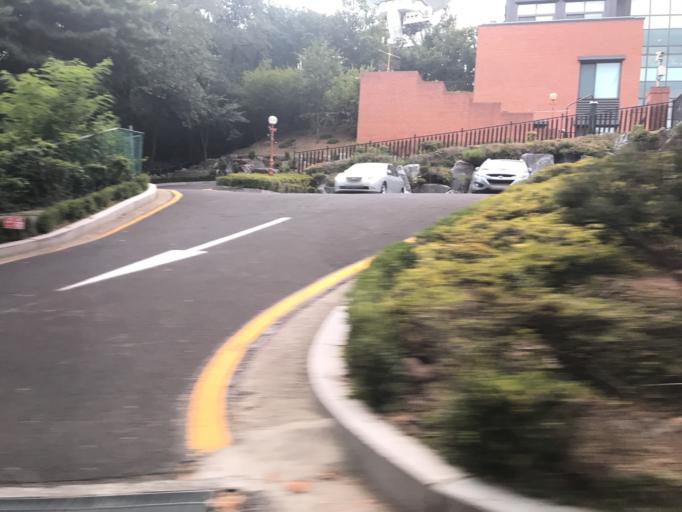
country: KR
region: Seoul
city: Seoul
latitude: 37.5653
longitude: 126.9420
